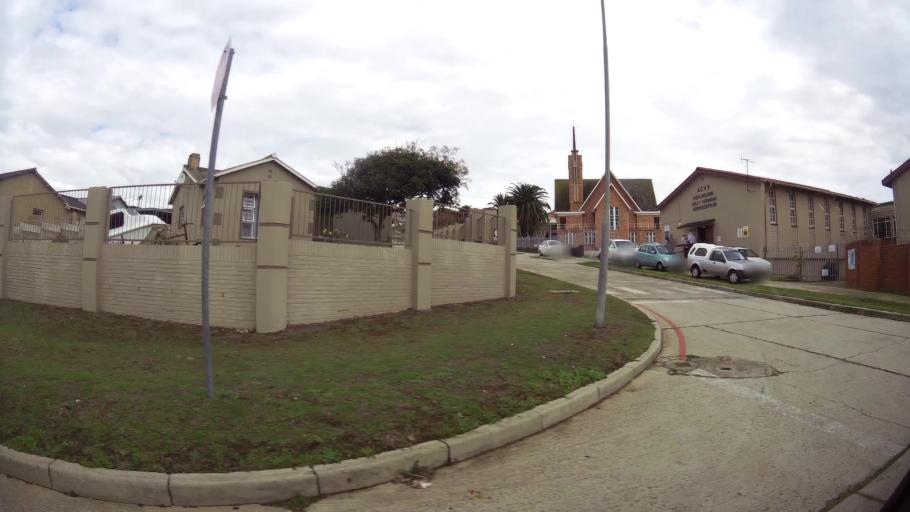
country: ZA
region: Eastern Cape
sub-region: Nelson Mandela Bay Metropolitan Municipality
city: Port Elizabeth
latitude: -33.9386
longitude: 25.5842
